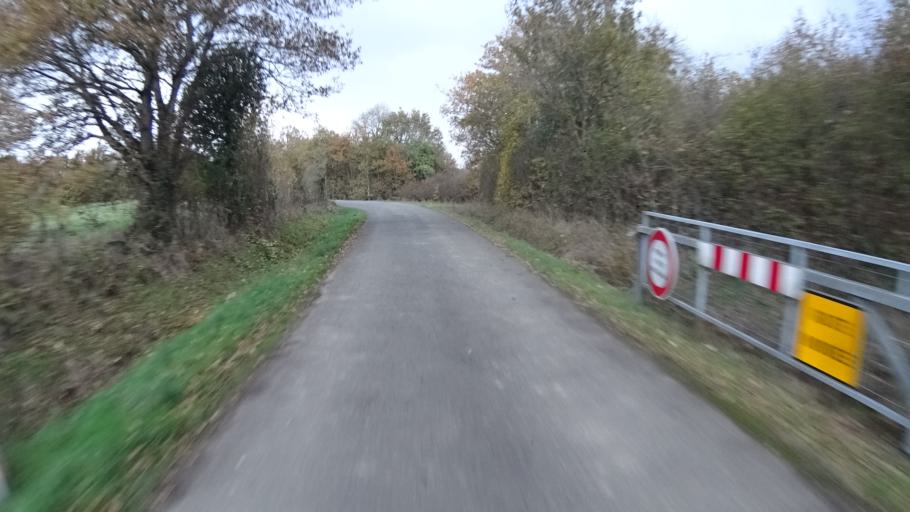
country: FR
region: Pays de la Loire
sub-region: Departement de la Loire-Atlantique
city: Avessac
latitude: 47.6638
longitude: -2.0253
